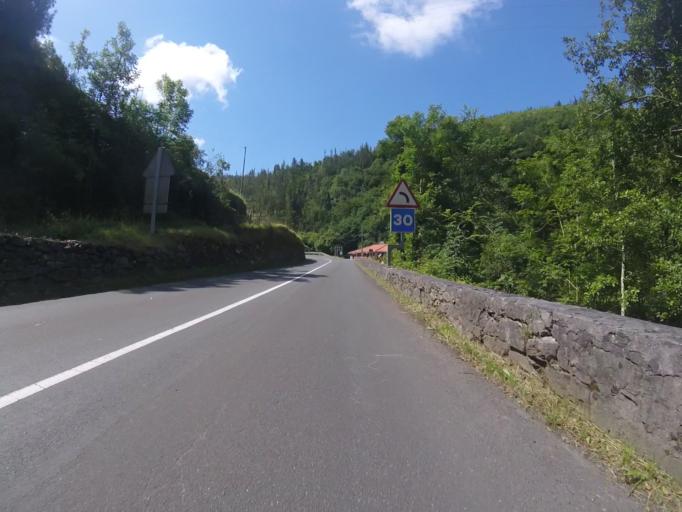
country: ES
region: Basque Country
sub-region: Provincia de Guipuzcoa
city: Azpeitia
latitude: 43.1774
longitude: -2.2237
